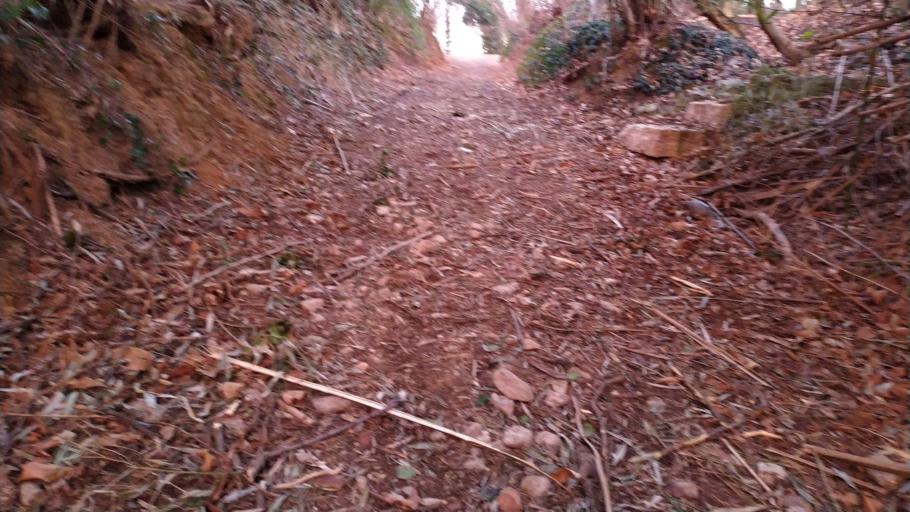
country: IT
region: Veneto
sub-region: Provincia di Treviso
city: Cornuda
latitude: 45.8394
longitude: 11.9992
